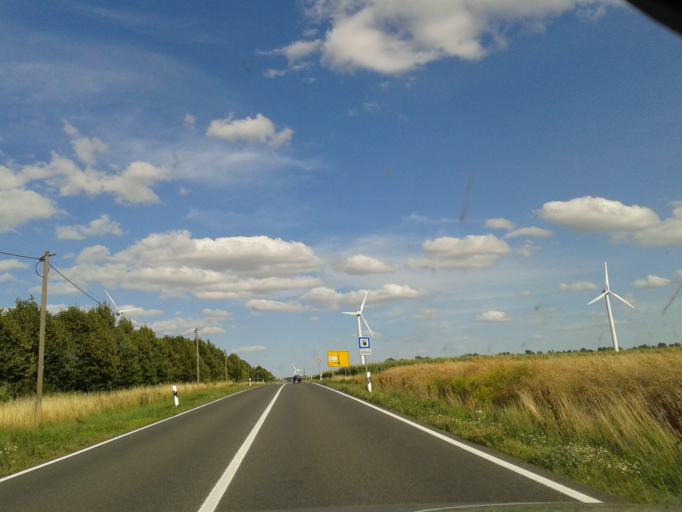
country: DE
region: Saxony-Anhalt
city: Polleben
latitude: 51.5769
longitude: 11.6127
